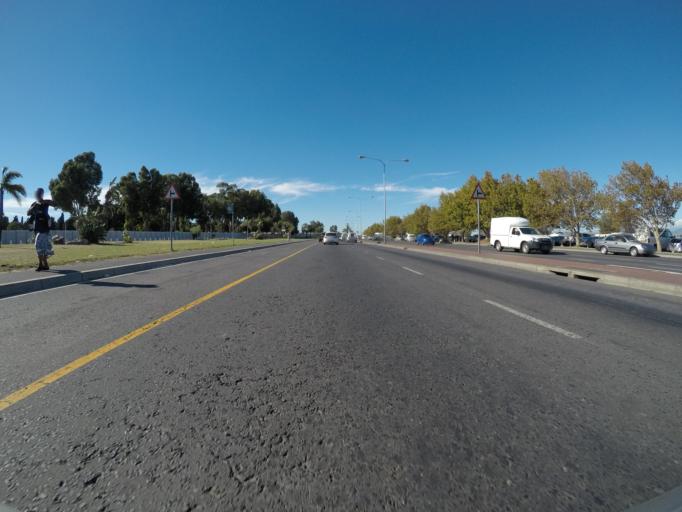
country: ZA
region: Western Cape
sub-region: City of Cape Town
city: Kraaifontein
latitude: -33.9109
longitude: 18.6656
